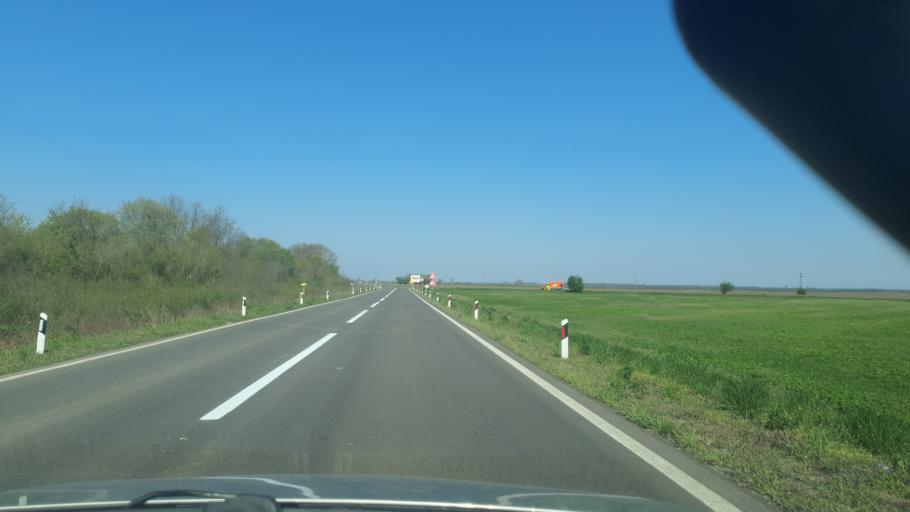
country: RS
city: Kolut
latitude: 45.8392
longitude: 18.9948
